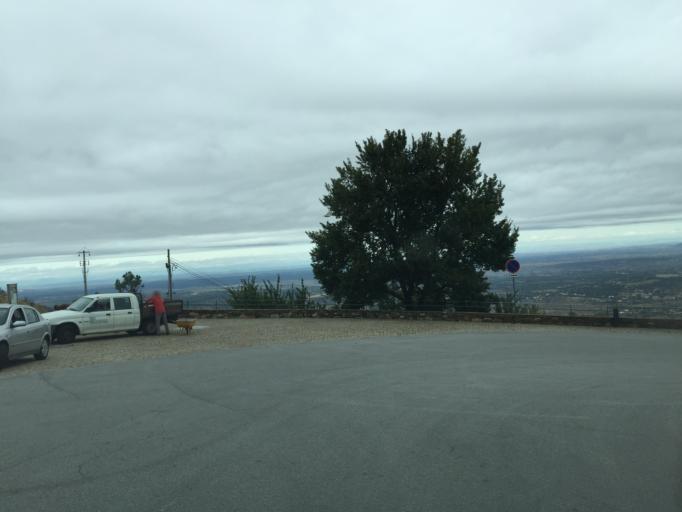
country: PT
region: Portalegre
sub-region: Marvao
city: Marvao
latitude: 39.3961
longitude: -7.3776
